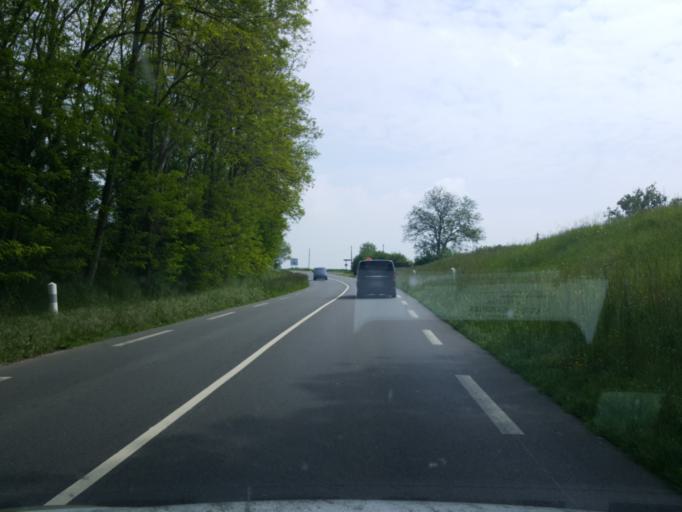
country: FR
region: Ile-de-France
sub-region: Departement du Val-d'Oise
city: Magny-en-Vexin
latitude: 49.0893
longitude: 1.7906
